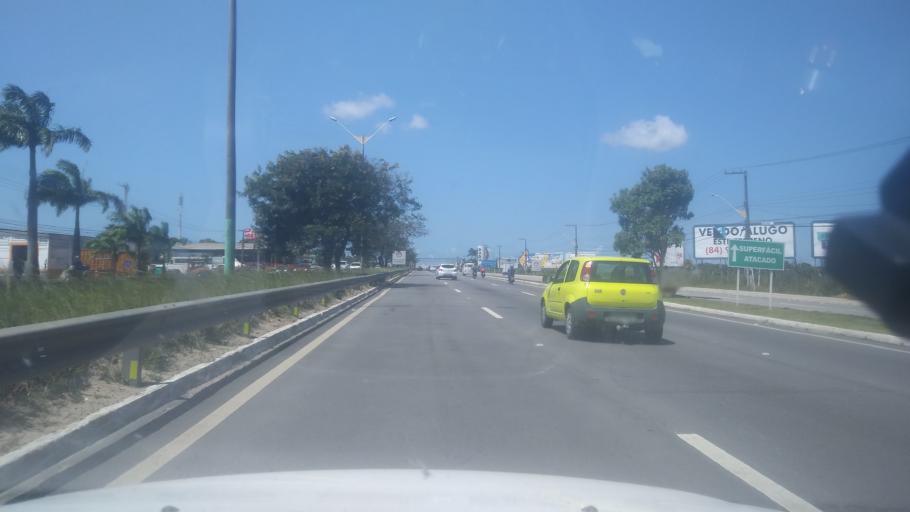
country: BR
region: Rio Grande do Norte
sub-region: Parnamirim
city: Parnamirim
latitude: -5.8904
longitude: -35.2512
